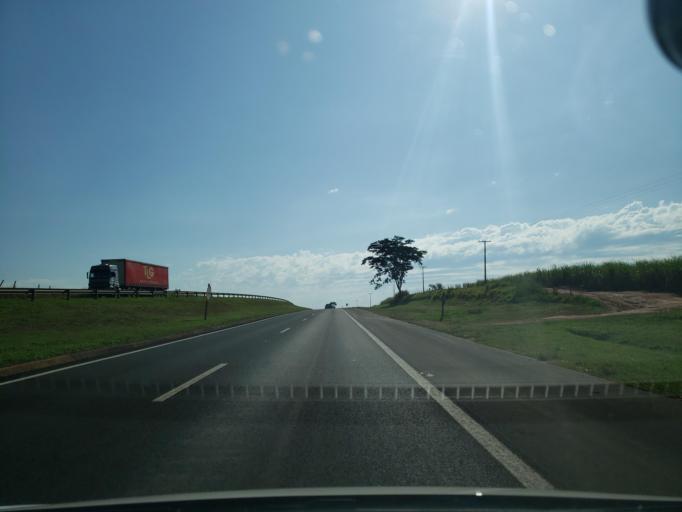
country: BR
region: Sao Paulo
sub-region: Penapolis
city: Penapolis
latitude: -21.5248
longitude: -49.9933
